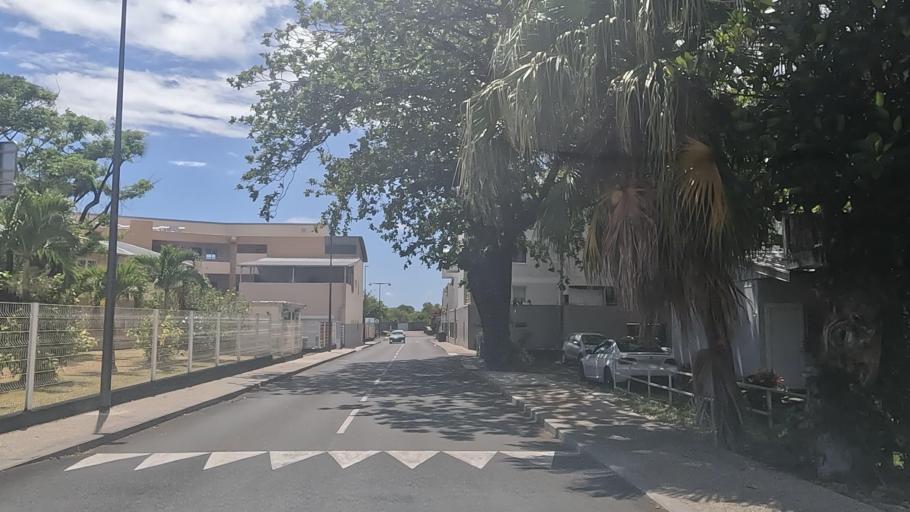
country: RE
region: Reunion
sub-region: Reunion
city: Saint-Benoit
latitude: -21.0314
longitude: 55.7143
